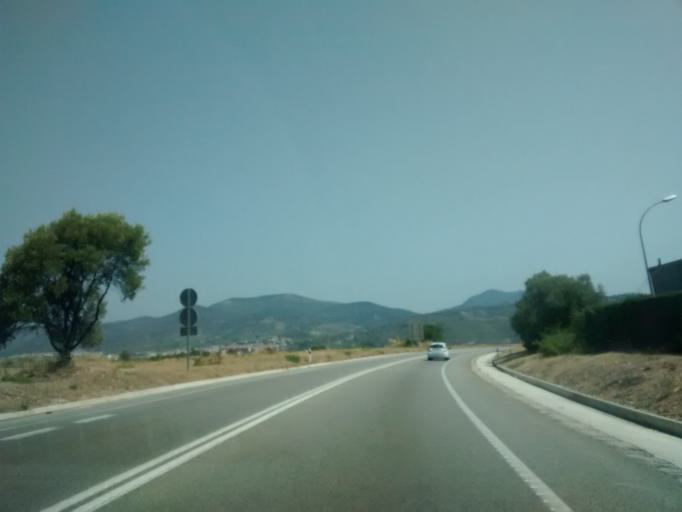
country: ES
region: Catalonia
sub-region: Provincia de Barcelona
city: Abrera
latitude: 41.5219
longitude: 1.8982
